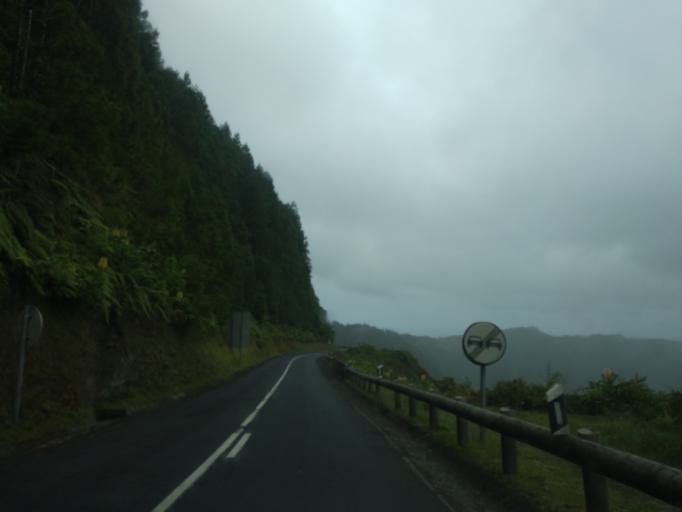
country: PT
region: Azores
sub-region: Ponta Delgada
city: Arrifes
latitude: 37.8385
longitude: -25.7881
